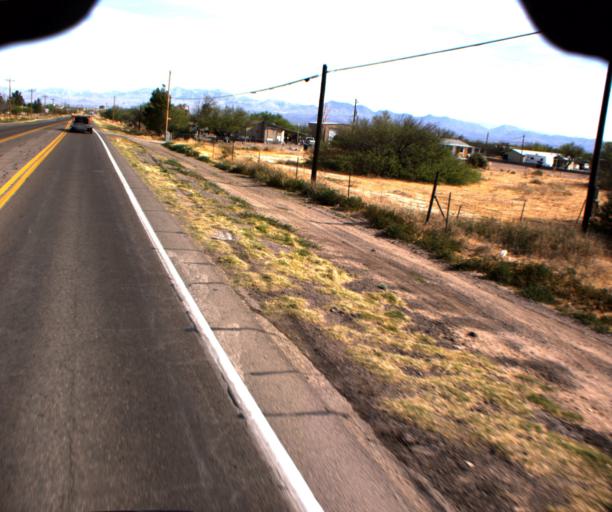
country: US
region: Arizona
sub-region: Graham County
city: Cactus Flat
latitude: 32.7662
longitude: -109.7163
